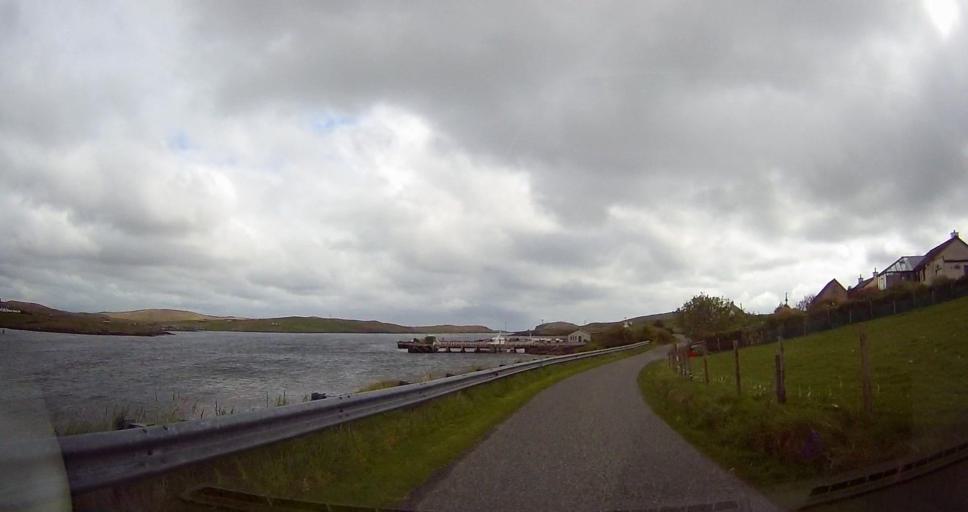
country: GB
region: Scotland
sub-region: Shetland Islands
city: Sandwick
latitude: 60.2261
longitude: -1.5696
